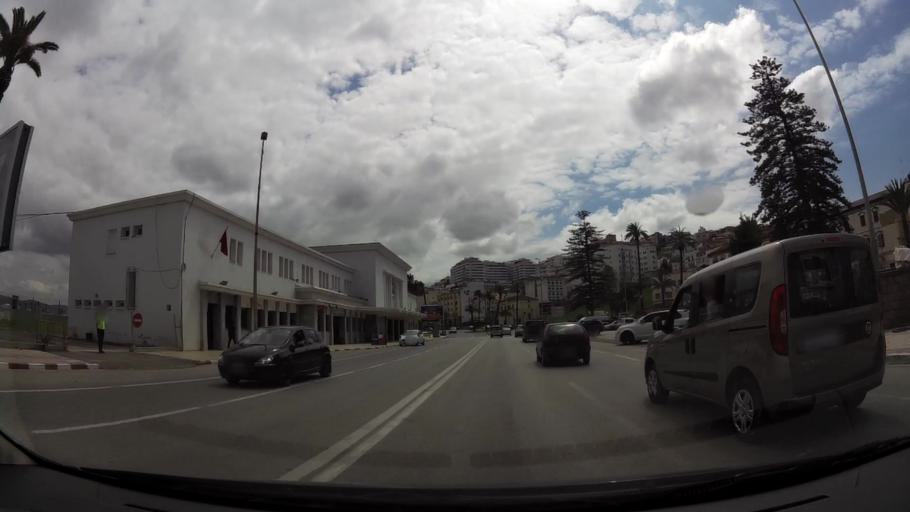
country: MA
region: Tanger-Tetouan
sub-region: Tanger-Assilah
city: Tangier
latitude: 35.7840
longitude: -5.8078
